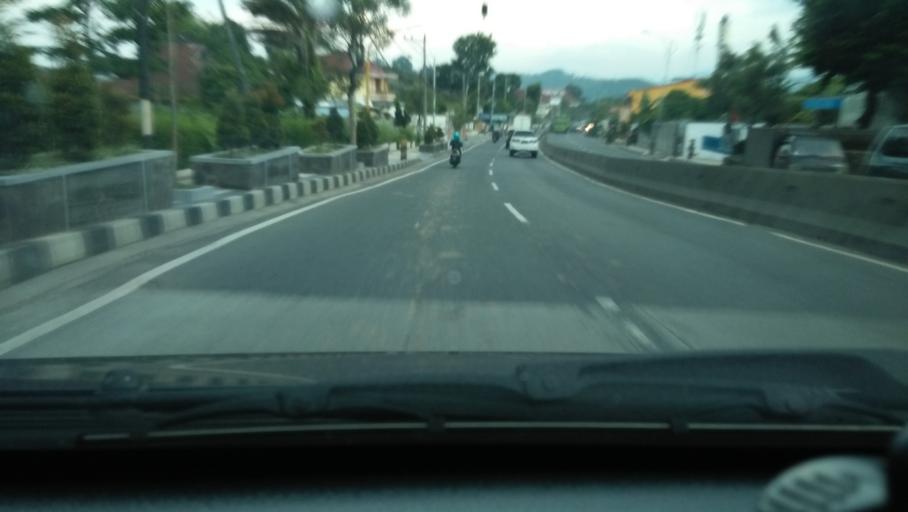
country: ID
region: Central Java
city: Ungaran
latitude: -7.1140
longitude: 110.4130
